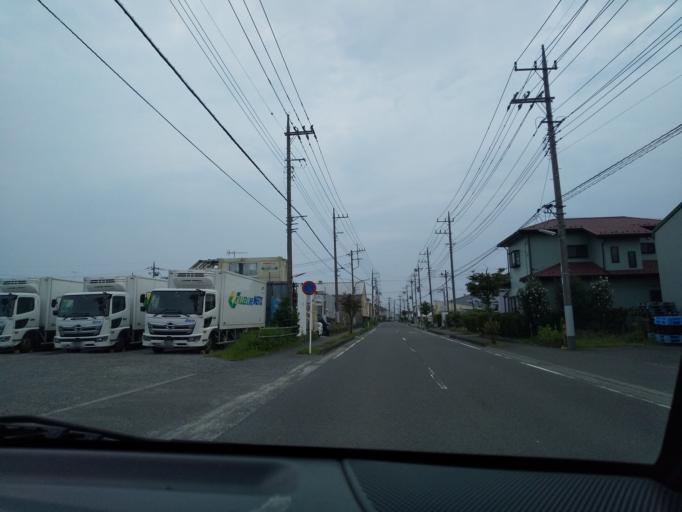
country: JP
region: Kanagawa
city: Atsugi
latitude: 35.4024
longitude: 139.3865
